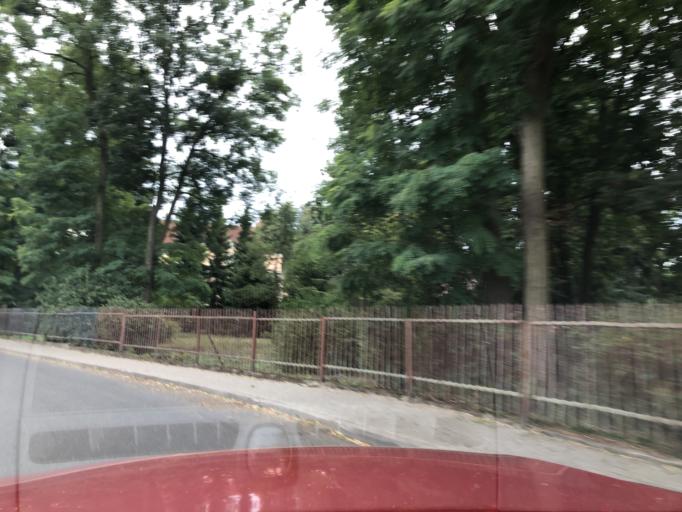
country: PL
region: Greater Poland Voivodeship
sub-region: Powiat szamotulski
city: Pniewy
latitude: 52.5100
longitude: 16.2506
